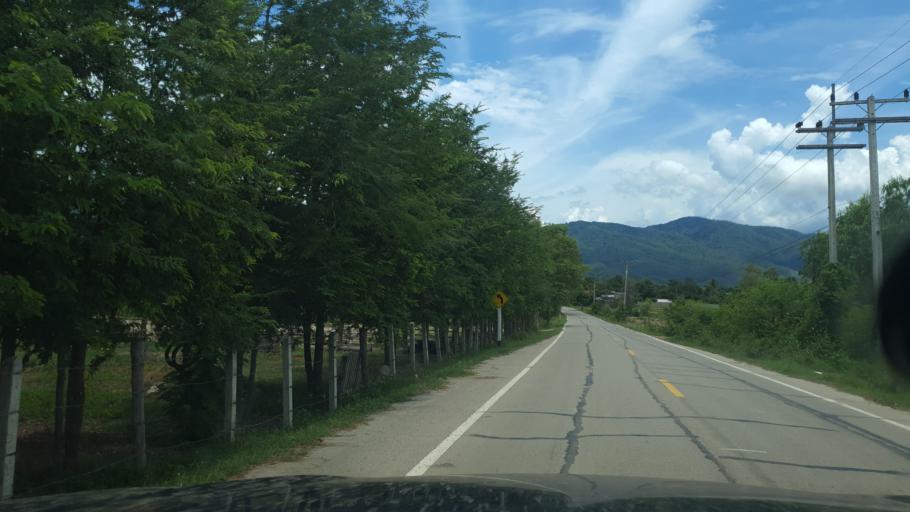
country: TH
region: Lampang
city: Sop Prap
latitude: 17.9148
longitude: 99.4117
